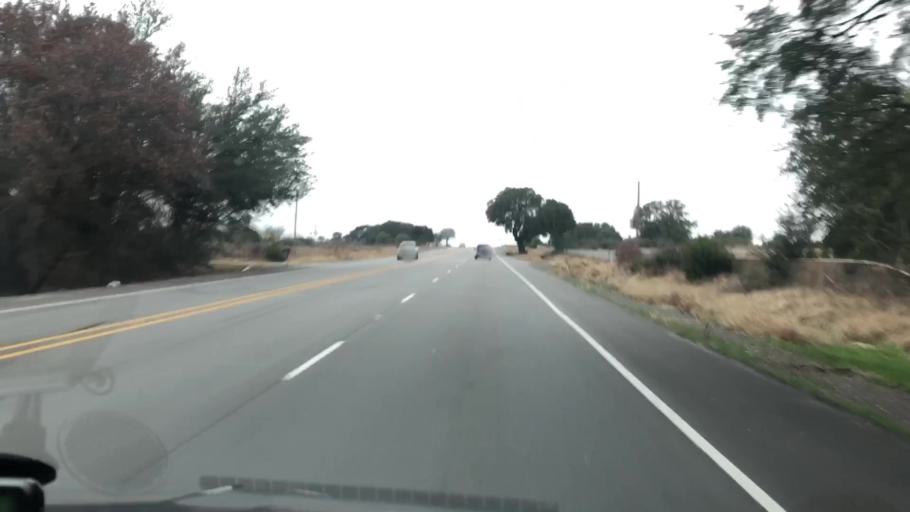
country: US
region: Texas
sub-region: Hamilton County
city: Hico
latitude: 32.0012
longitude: -98.0518
